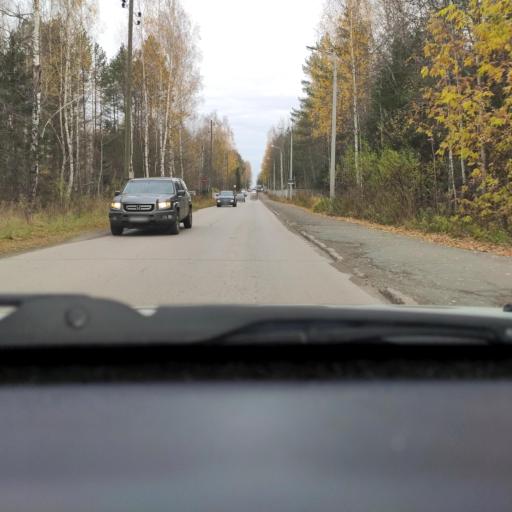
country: RU
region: Perm
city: Kondratovo
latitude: 58.0614
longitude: 56.1247
